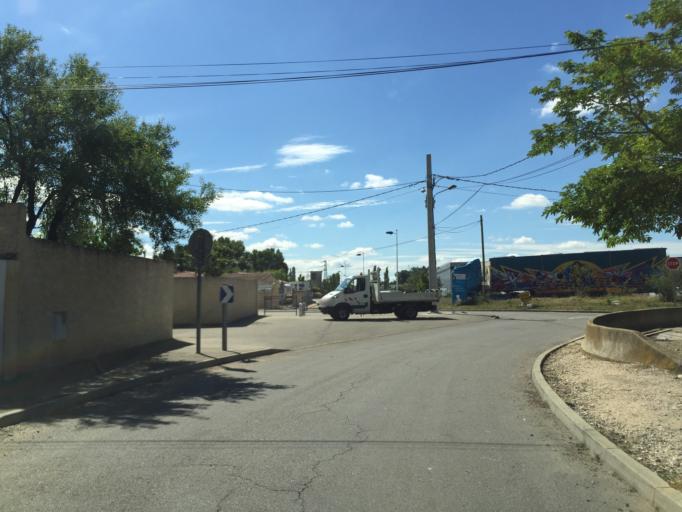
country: FR
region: Provence-Alpes-Cote d'Azur
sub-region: Departement du Vaucluse
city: Vedene
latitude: 43.9947
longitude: 4.8938
